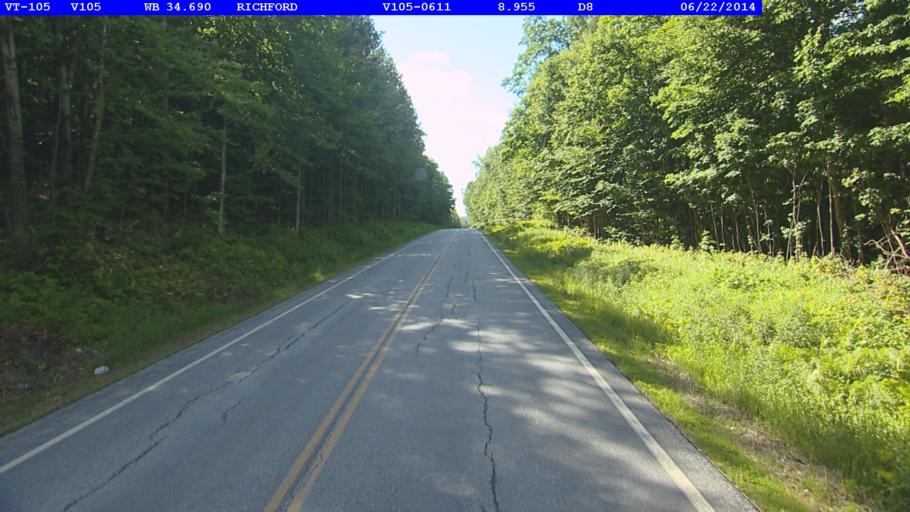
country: US
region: Vermont
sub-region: Franklin County
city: Richford
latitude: 44.9877
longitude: -72.5543
